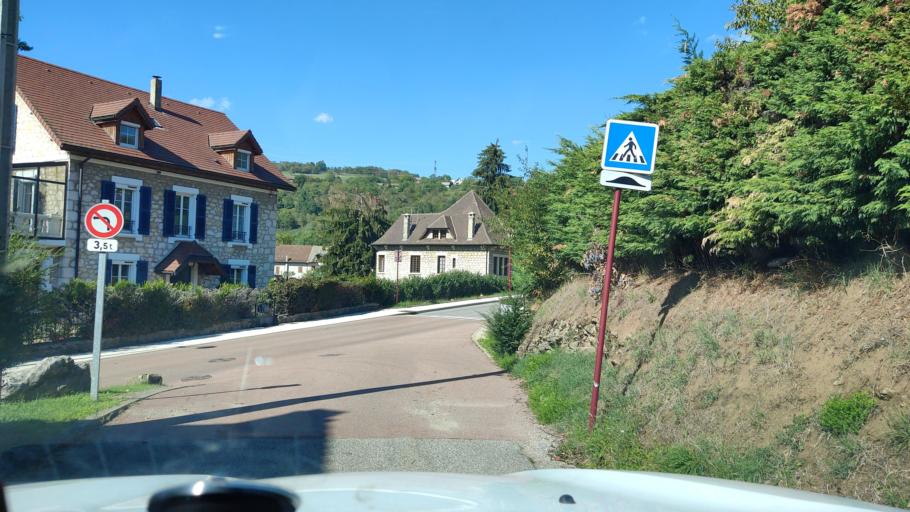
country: FR
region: Rhone-Alpes
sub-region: Departement de la Savoie
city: La Bridoire
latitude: 45.5301
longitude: 5.7425
